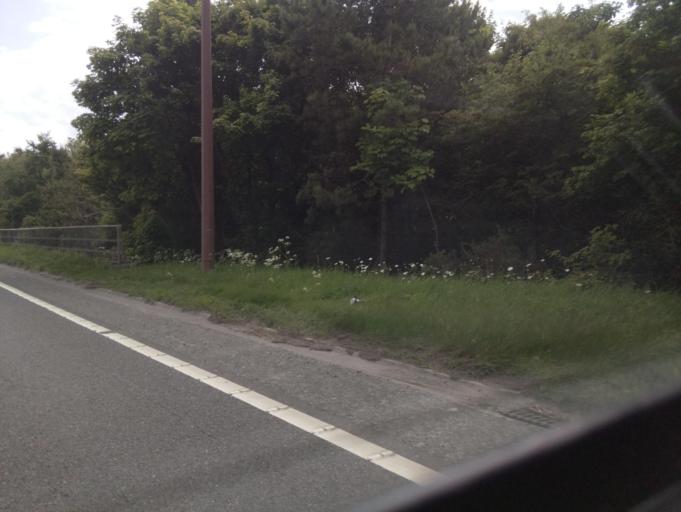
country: GB
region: England
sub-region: County Durham
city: Shotton
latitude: 54.7796
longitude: -1.3608
